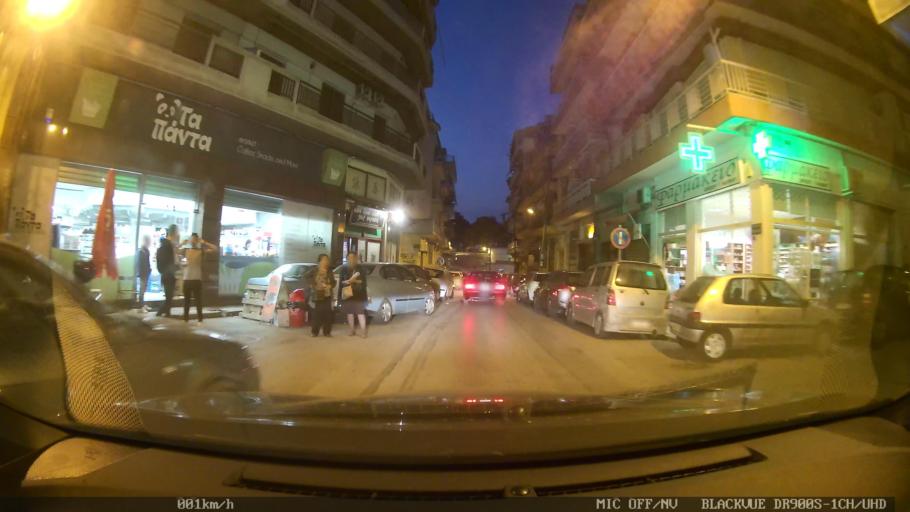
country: GR
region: Central Macedonia
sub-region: Nomos Thessalonikis
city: Triandria
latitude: 40.6216
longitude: 22.9581
